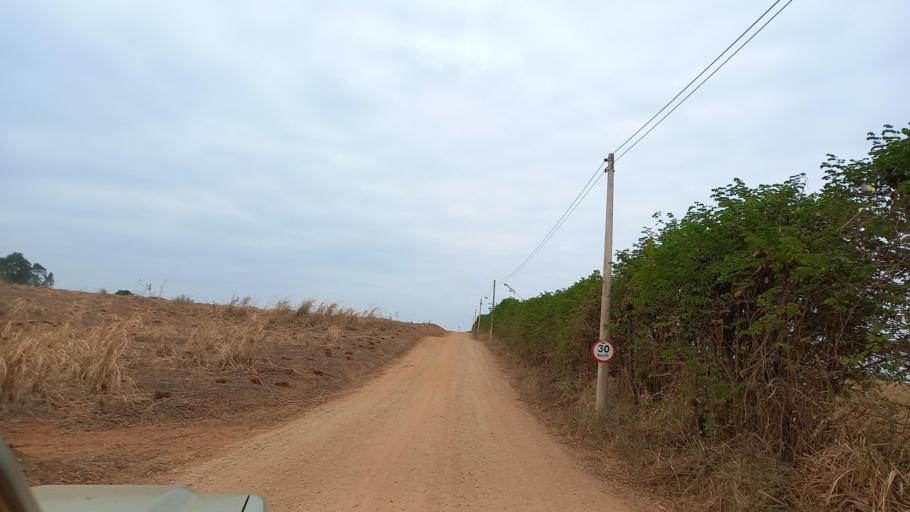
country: BR
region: Sao Paulo
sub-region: Moji-Guacu
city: Mogi-Gaucu
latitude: -22.2774
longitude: -46.8448
